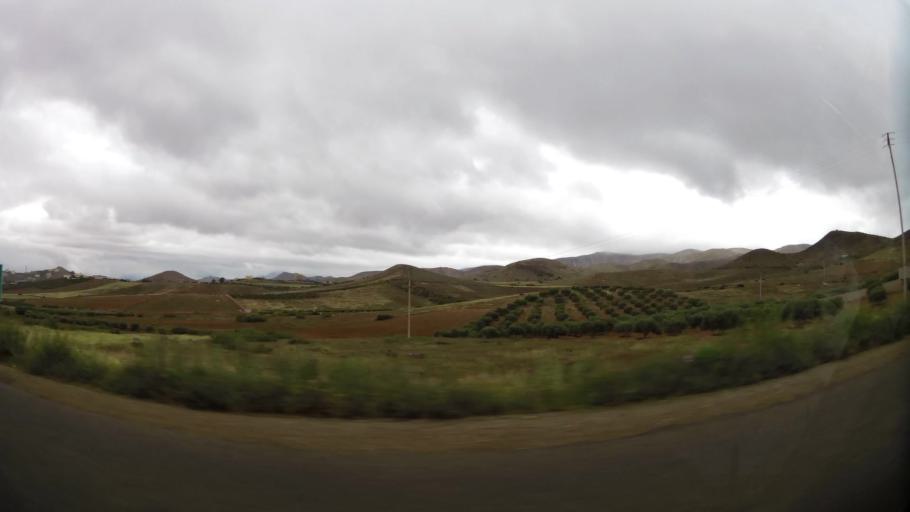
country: MA
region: Oriental
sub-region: Nador
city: Midar
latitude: 35.0629
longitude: -3.4696
